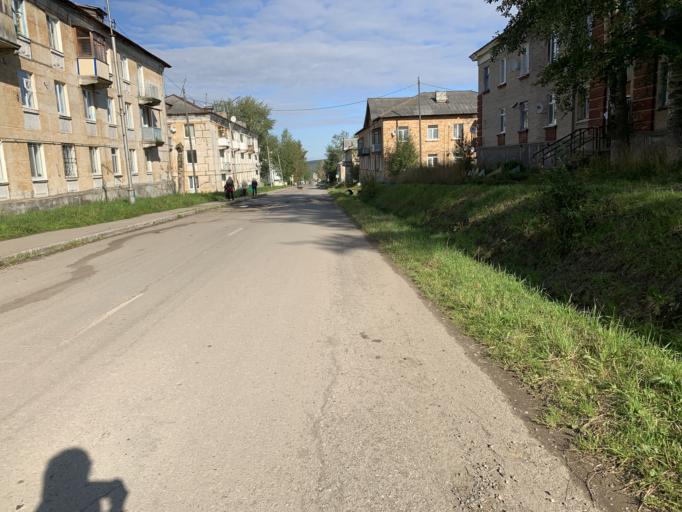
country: RU
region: Perm
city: Gubakha
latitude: 58.8391
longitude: 57.5561
